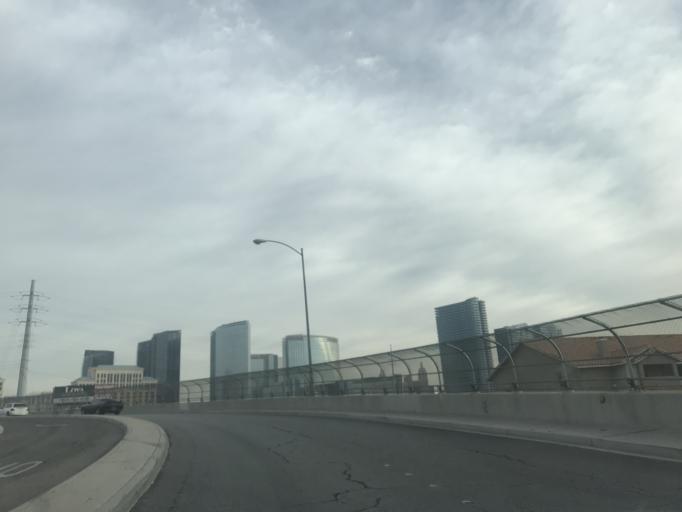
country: US
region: Nevada
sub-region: Clark County
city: Paradise
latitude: 36.1143
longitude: -115.1869
